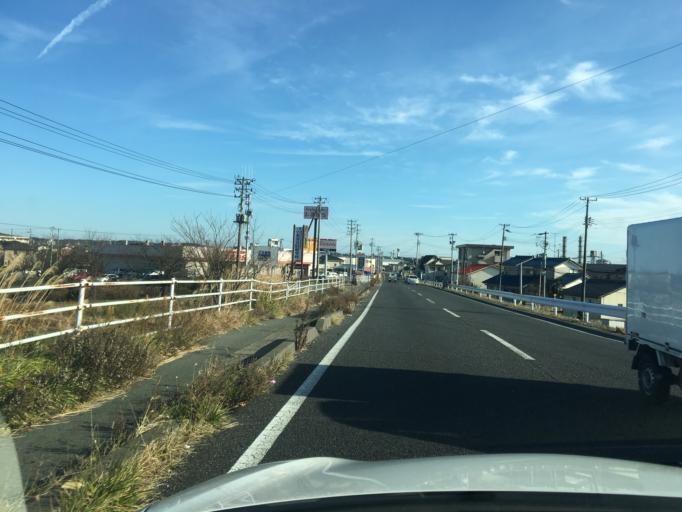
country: JP
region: Fukushima
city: Iwaki
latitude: 36.9499
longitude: 140.8815
